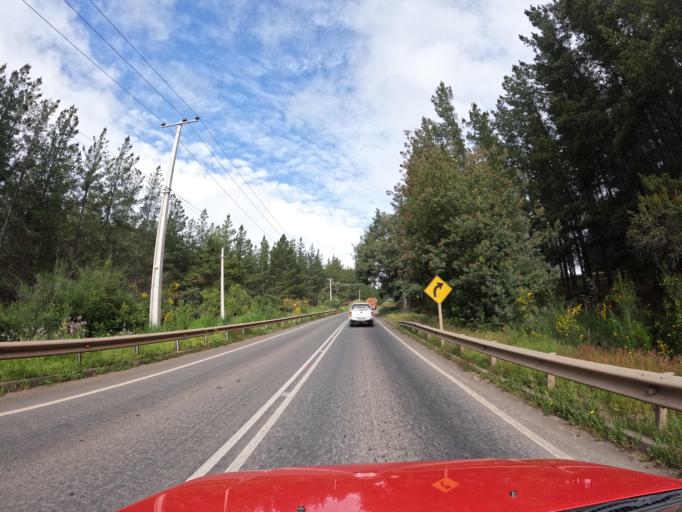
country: CL
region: O'Higgins
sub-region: Provincia de Colchagua
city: Santa Cruz
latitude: -34.3530
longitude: -71.9249
